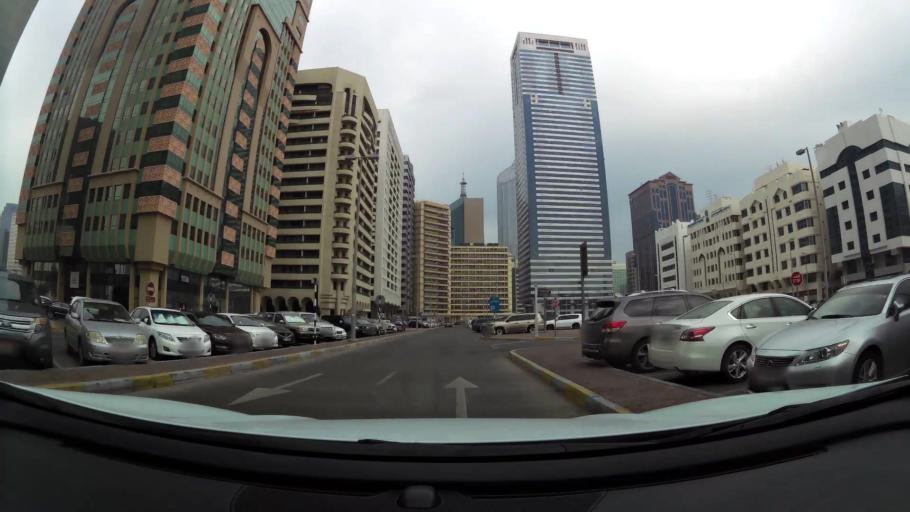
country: AE
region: Abu Dhabi
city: Abu Dhabi
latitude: 24.4813
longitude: 54.3616
